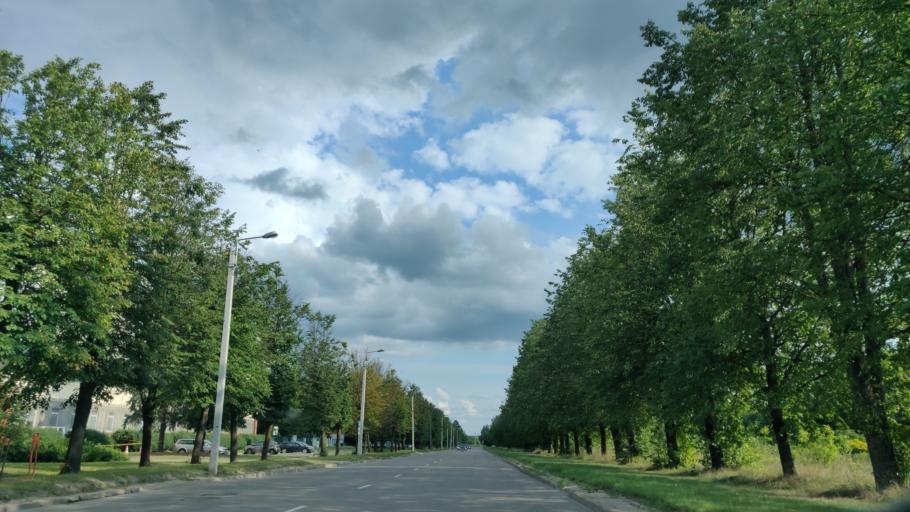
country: LT
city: Baltoji Voke
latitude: 54.6238
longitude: 25.1413
